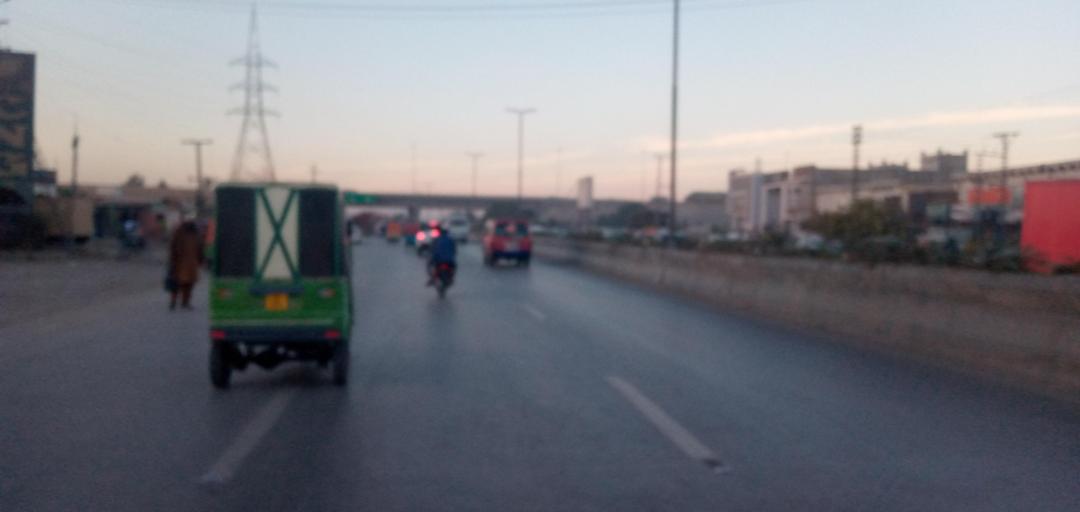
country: PK
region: Khyber Pakhtunkhwa
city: Peshawar
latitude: 34.0218
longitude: 71.6214
